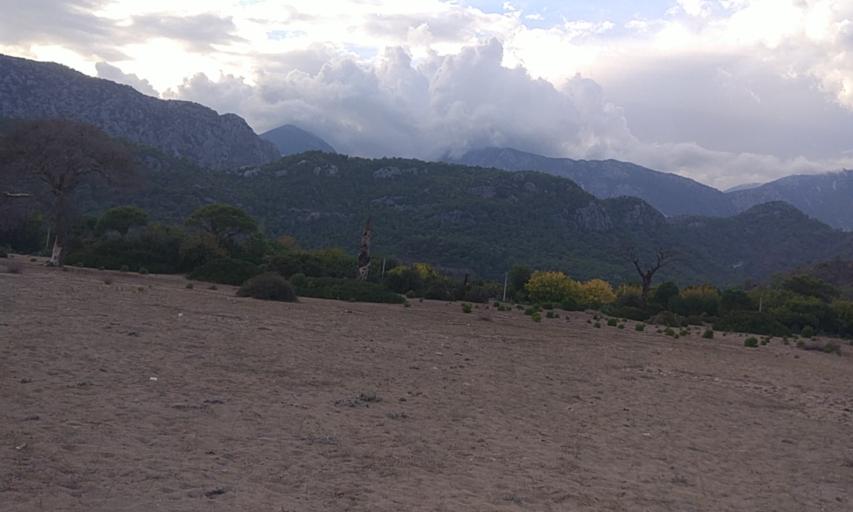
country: TR
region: Antalya
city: Tekirova
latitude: 36.4194
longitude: 30.4849
